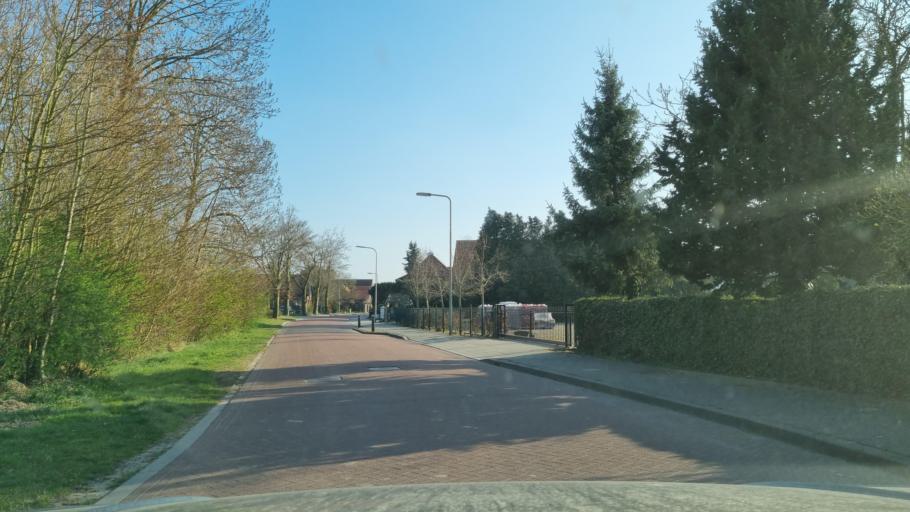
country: NL
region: Limburg
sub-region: Gemeente Gennep
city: Gennep
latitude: 51.7177
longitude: 6.0254
